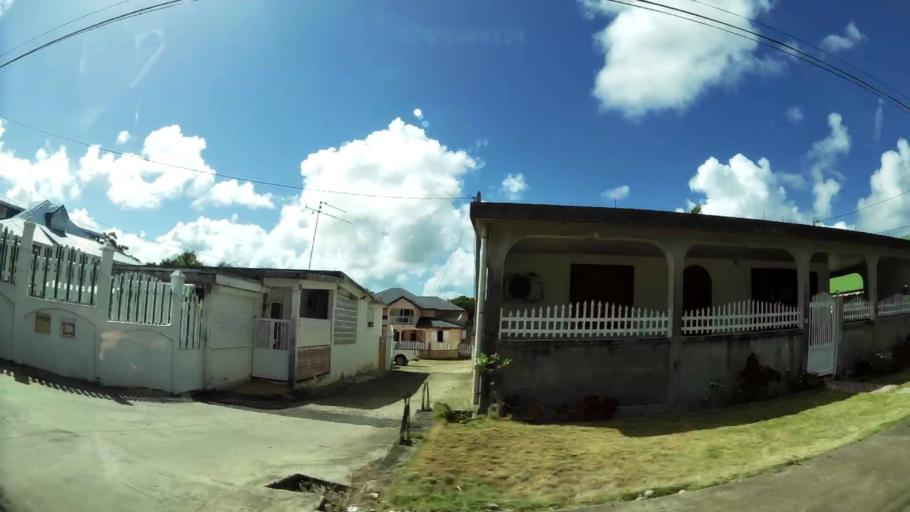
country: GP
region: Guadeloupe
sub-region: Guadeloupe
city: Anse-Bertrand
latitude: 16.4463
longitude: -61.4762
